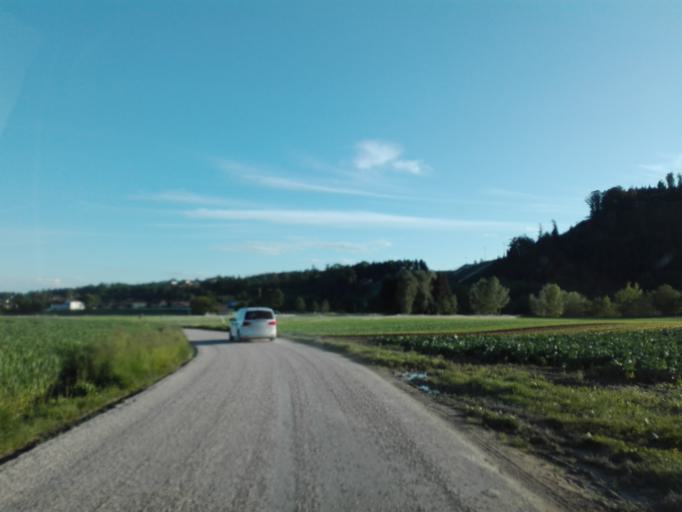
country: AT
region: Upper Austria
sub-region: Politischer Bezirk Urfahr-Umgebung
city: Feldkirchen an der Donau
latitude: 48.3295
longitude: 13.9995
